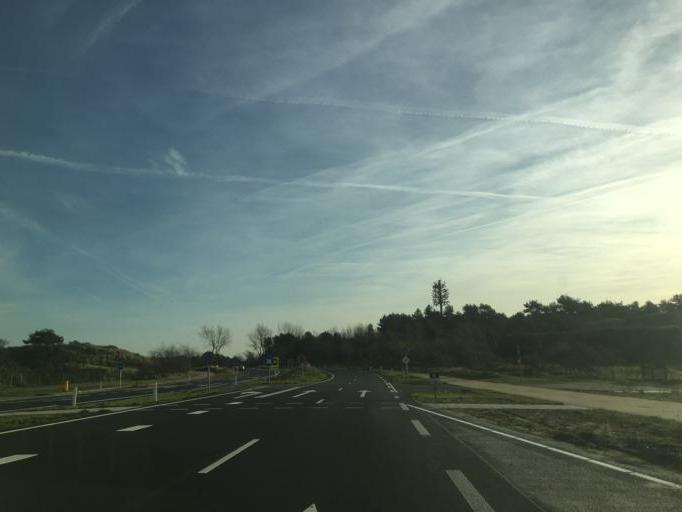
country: NL
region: North Holland
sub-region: Gemeente Zandvoort
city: Zandvoort
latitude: 52.4014
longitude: 4.5583
